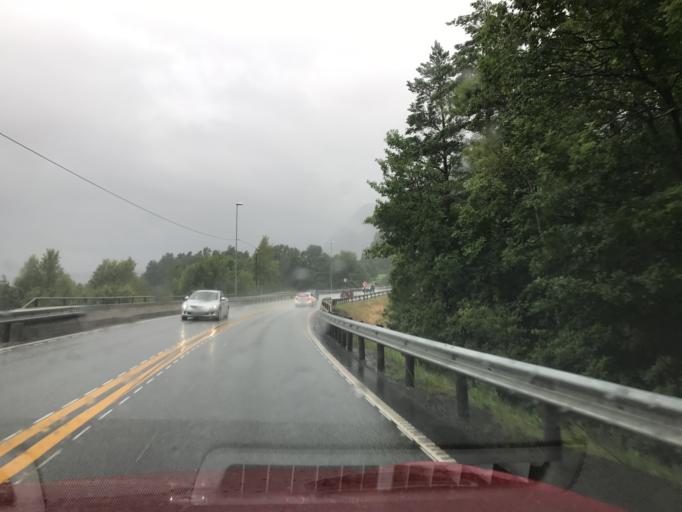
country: NO
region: Rogaland
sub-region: Lund
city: Moi
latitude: 58.4029
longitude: 6.6233
